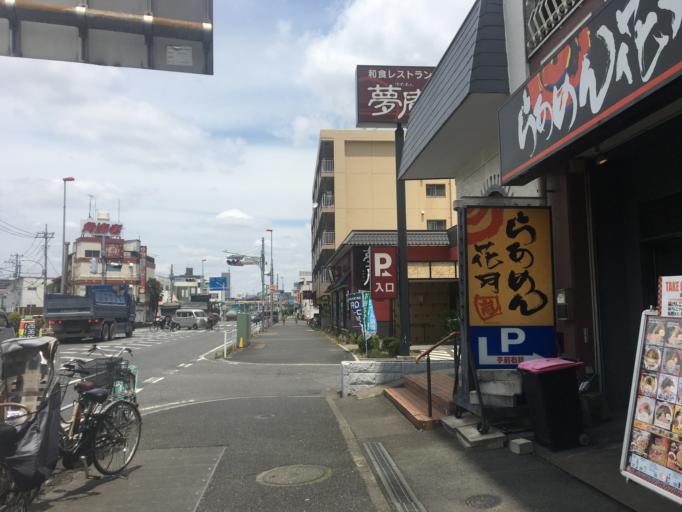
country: JP
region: Saitama
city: Shimotoda
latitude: 35.8184
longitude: 139.6818
